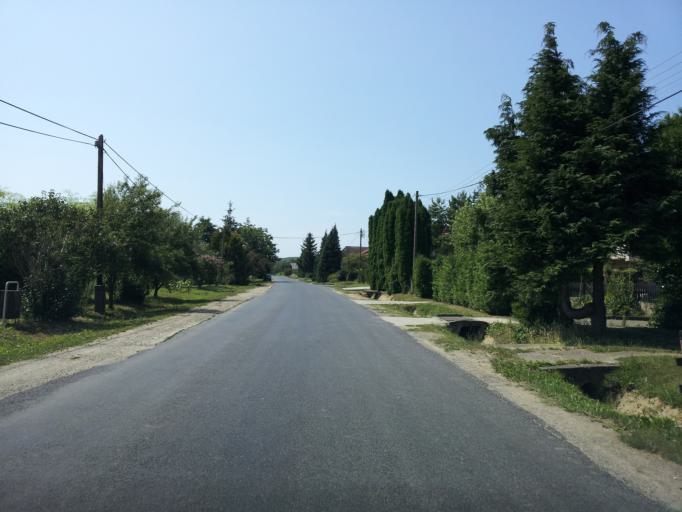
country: HU
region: Zala
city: Pacsa
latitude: 46.8105
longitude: 16.9847
